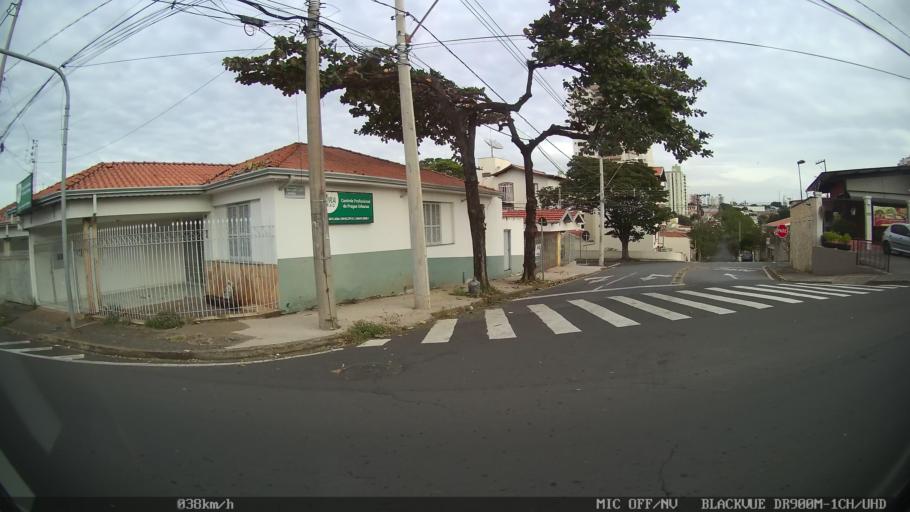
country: BR
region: Sao Paulo
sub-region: Piracicaba
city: Piracicaba
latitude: -22.7259
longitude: -47.6305
